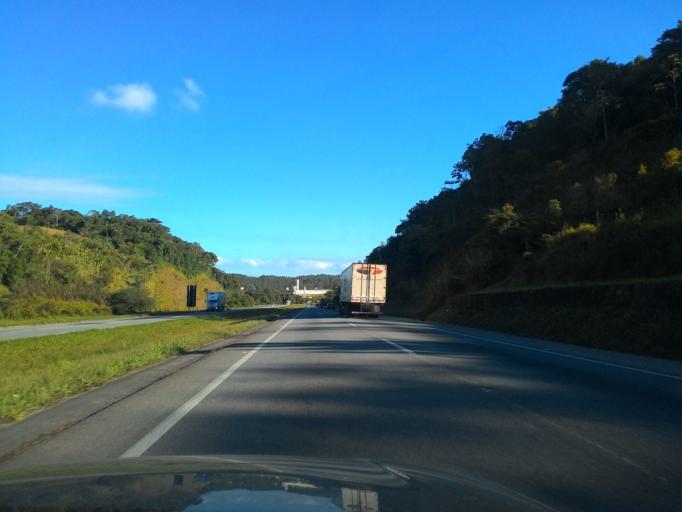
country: BR
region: Sao Paulo
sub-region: Registro
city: Registro
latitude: -24.5565
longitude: -47.8659
